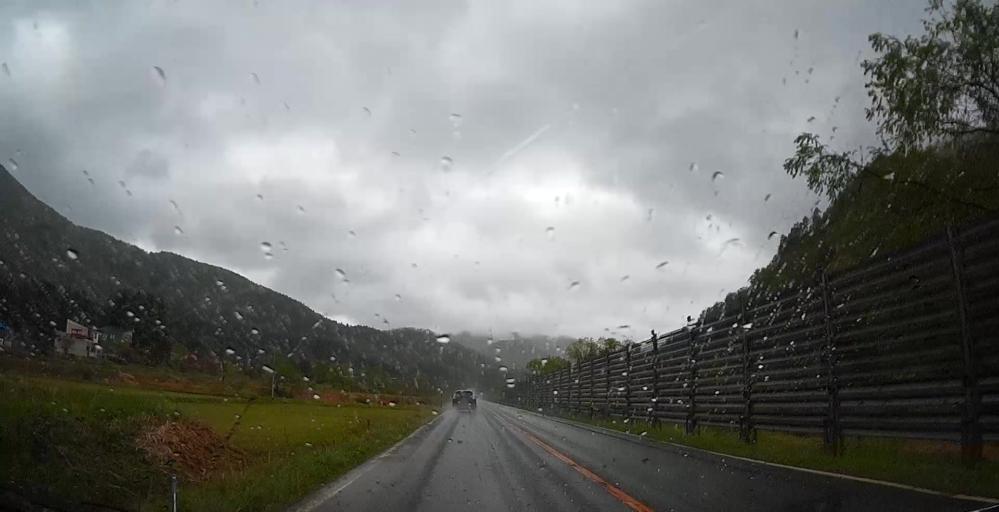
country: JP
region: Yamagata
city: Nagai
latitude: 38.0523
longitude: 139.8181
